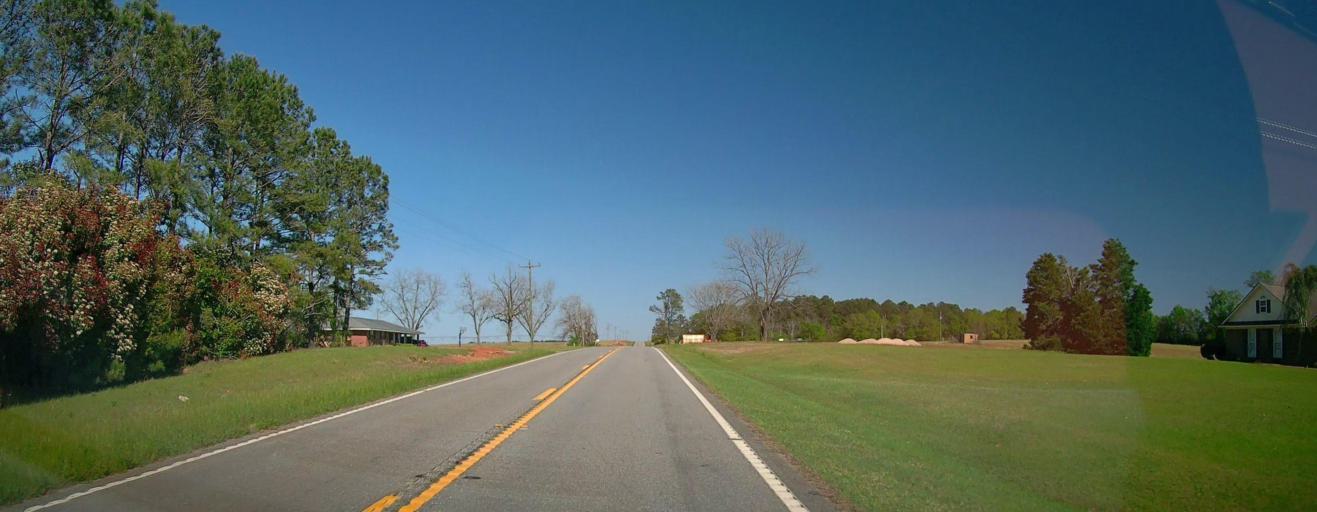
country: US
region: Georgia
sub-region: Dooly County
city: Unadilla
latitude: 32.2600
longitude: -83.6808
